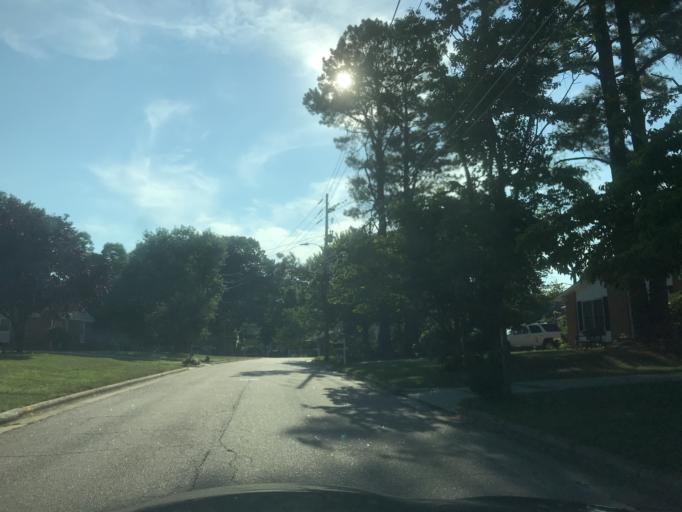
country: US
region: North Carolina
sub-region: Wake County
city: West Raleigh
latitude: 35.8506
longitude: -78.6295
